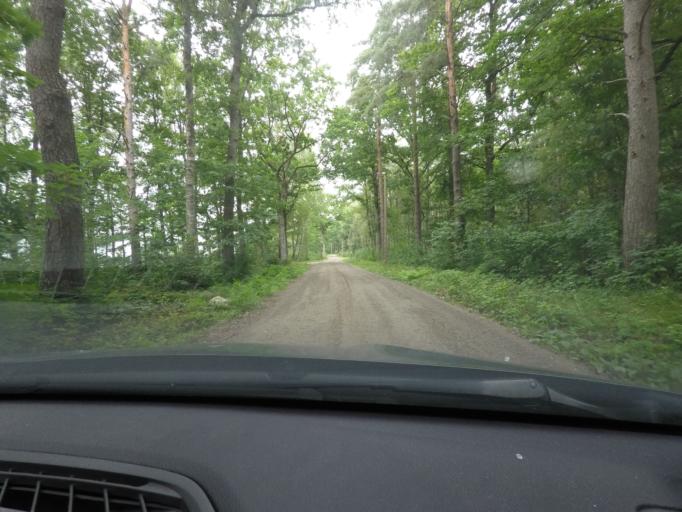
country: SE
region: Skane
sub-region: Osby Kommun
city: Osby
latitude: 56.3547
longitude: 13.9939
